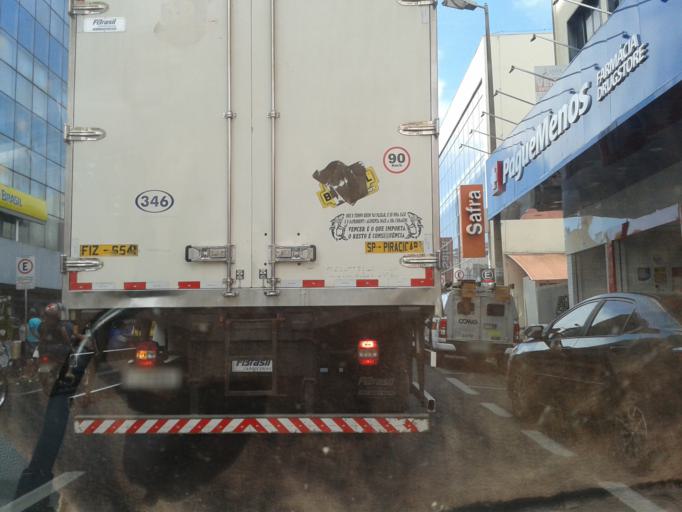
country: BR
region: Minas Gerais
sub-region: Uberlandia
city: Uberlandia
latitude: -18.9172
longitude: -48.2770
